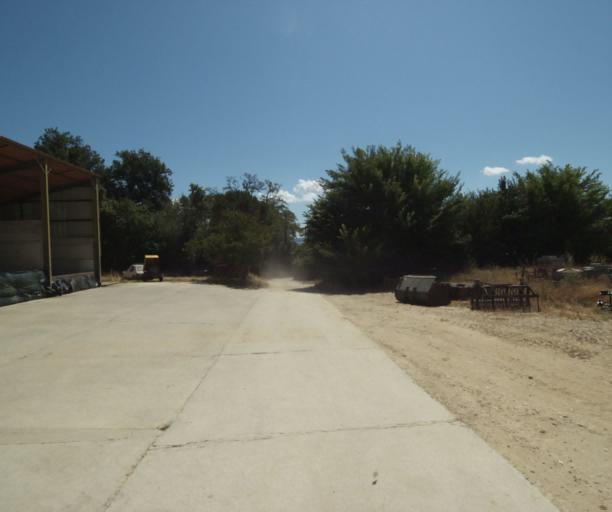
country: FR
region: Midi-Pyrenees
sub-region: Departement de la Haute-Garonne
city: Saint-Felix-Lauragais
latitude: 43.4869
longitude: 1.9282
